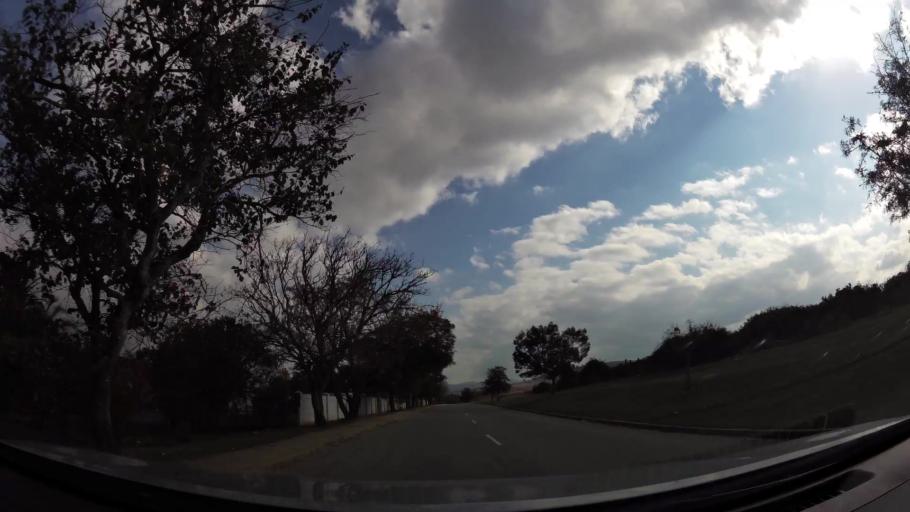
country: ZA
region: Eastern Cape
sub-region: Nelson Mandela Bay Metropolitan Municipality
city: Uitenhage
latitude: -33.7308
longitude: 25.4107
